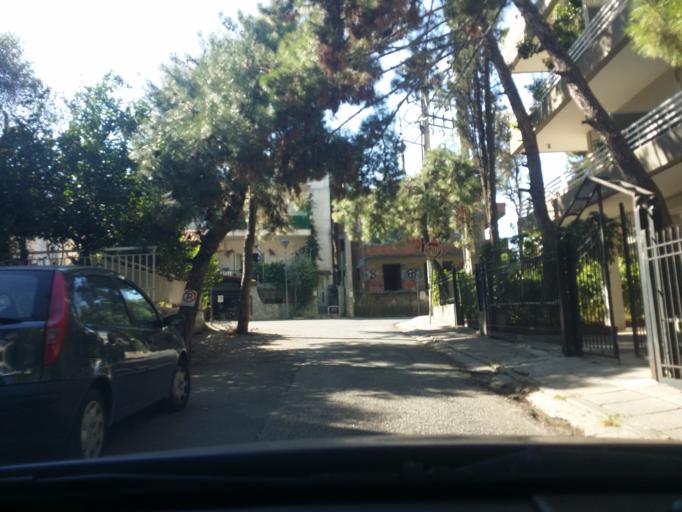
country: GR
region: Attica
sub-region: Nomarchia Athinas
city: Agia Paraskevi
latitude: 38.0162
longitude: 23.8359
